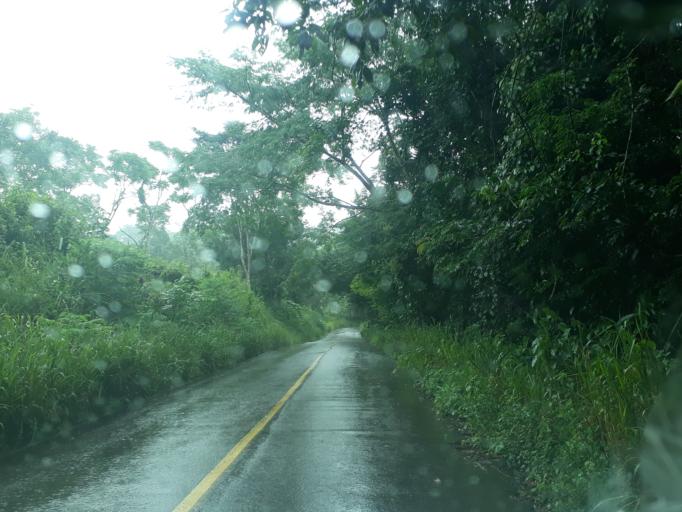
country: CO
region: Cundinamarca
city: Paratebueno
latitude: 4.4022
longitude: -73.3046
